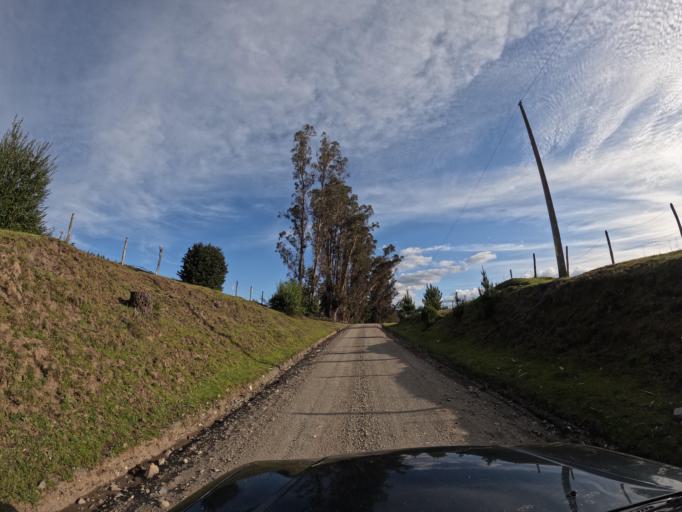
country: CL
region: Biobio
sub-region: Provincia de Biobio
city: La Laja
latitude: -37.1993
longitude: -72.7670
